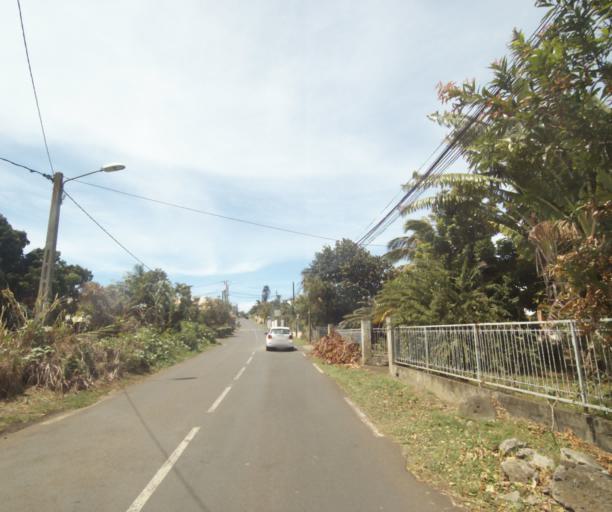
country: RE
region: Reunion
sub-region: Reunion
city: Saint-Paul
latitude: -21.0468
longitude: 55.2793
